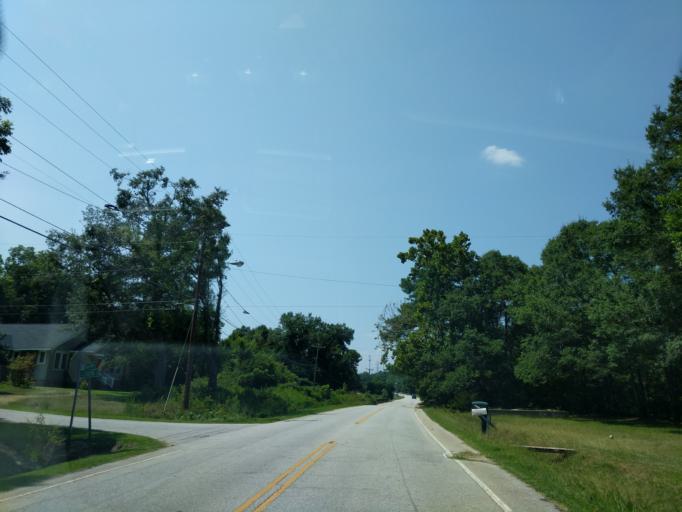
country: US
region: South Carolina
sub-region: Spartanburg County
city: Duncan
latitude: 34.9433
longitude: -82.1532
